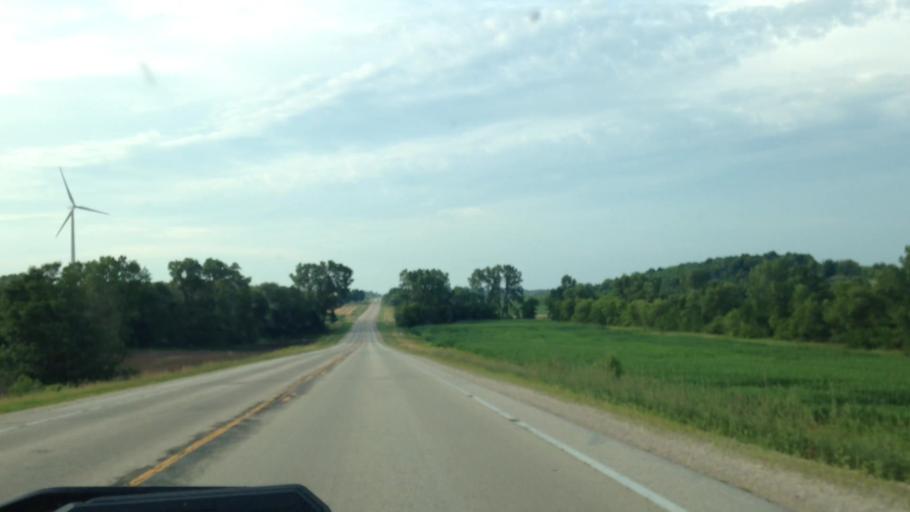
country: US
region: Wisconsin
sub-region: Dodge County
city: Theresa
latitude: 43.4375
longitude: -88.4503
